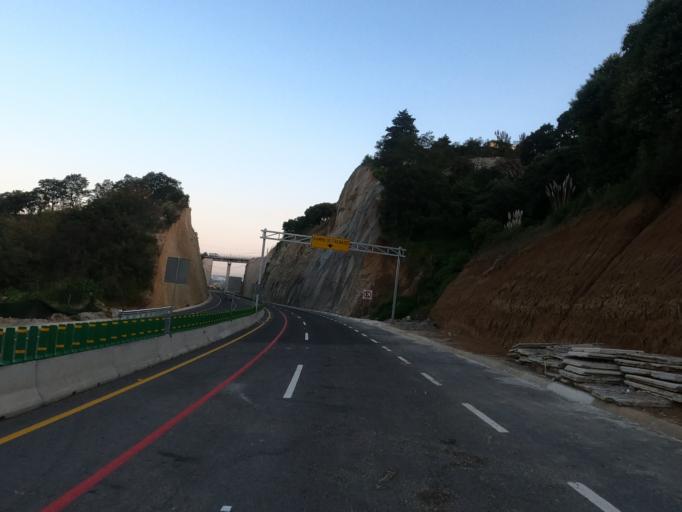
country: MX
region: Mexico
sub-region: Naucalpan de Juarez
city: Llano de las Flores (Barrio del Hueso)
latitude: 19.4236
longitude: -99.3302
